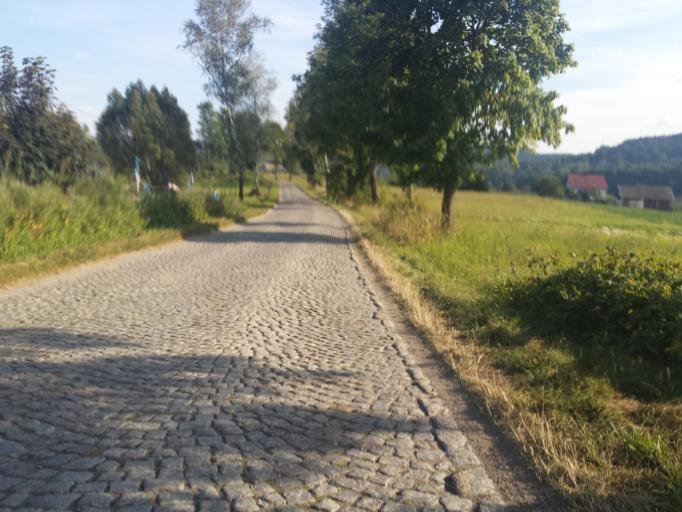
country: PL
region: Subcarpathian Voivodeship
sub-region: Powiat leski
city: Uherce Mineralne
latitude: 49.4477
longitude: 22.3924
